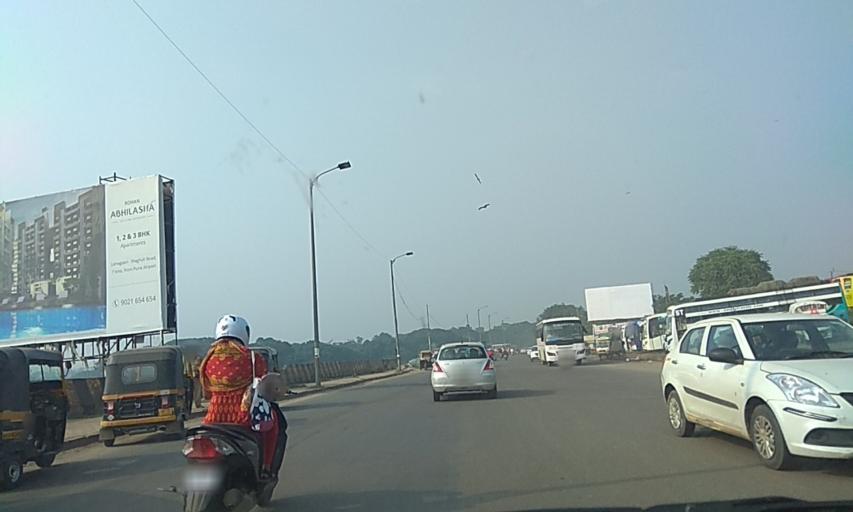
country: IN
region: Maharashtra
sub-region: Pune Division
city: Shivaji Nagar
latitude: 18.5339
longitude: 73.8611
